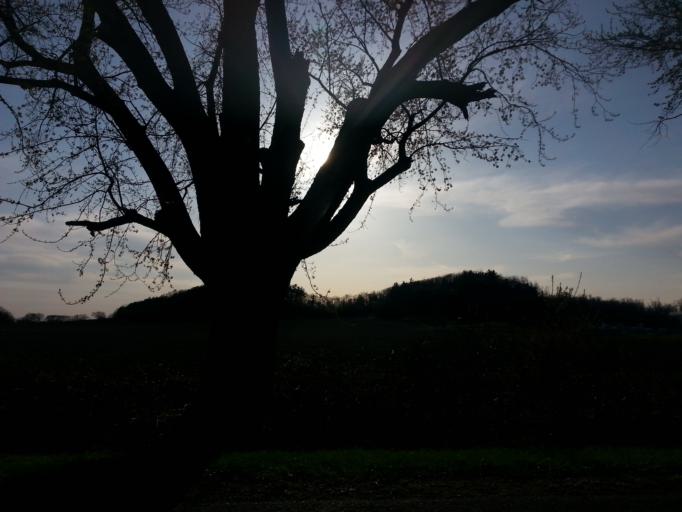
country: US
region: Minnesota
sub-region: Washington County
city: Afton
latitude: 44.8504
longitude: -92.7159
